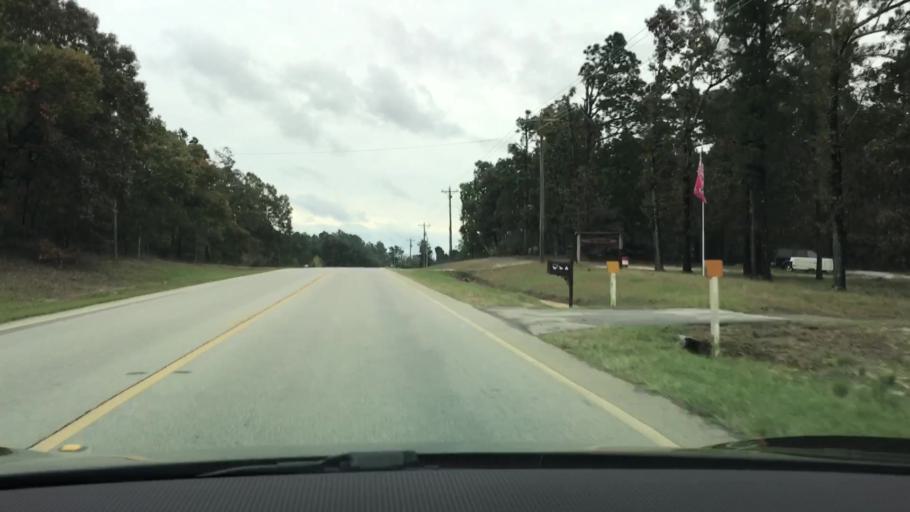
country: US
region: Georgia
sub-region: Jefferson County
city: Wrens
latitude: 33.1911
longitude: -82.4581
